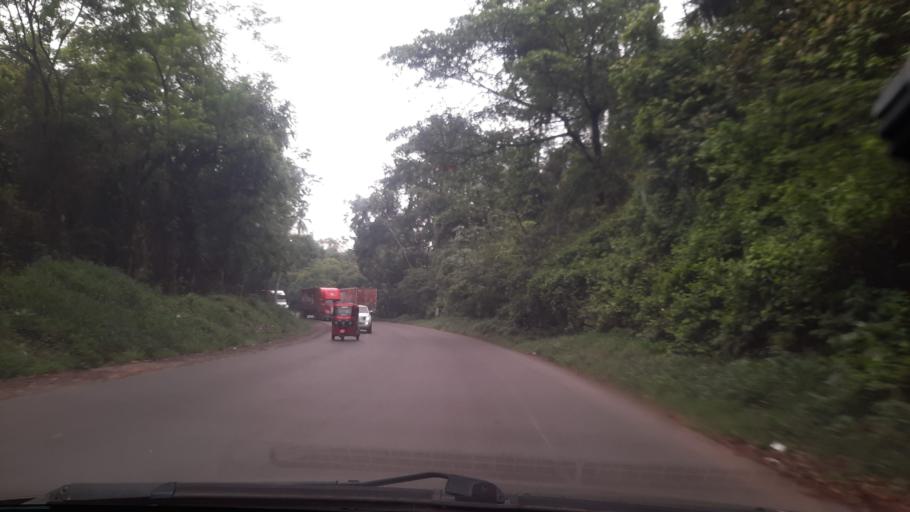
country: GT
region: Izabal
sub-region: Municipio de Los Amates
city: Los Amates
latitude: 15.2678
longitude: -89.0862
